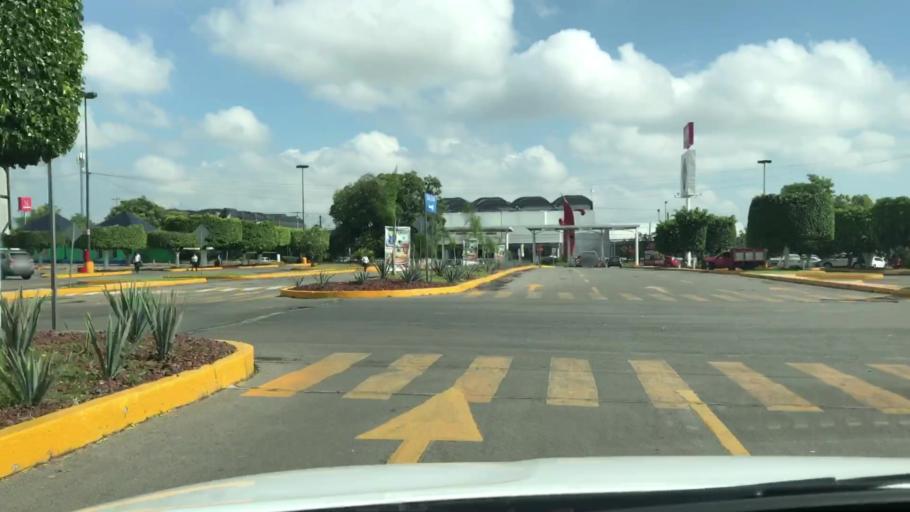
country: MX
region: Jalisco
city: Guadalajara
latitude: 20.6793
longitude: -103.4303
